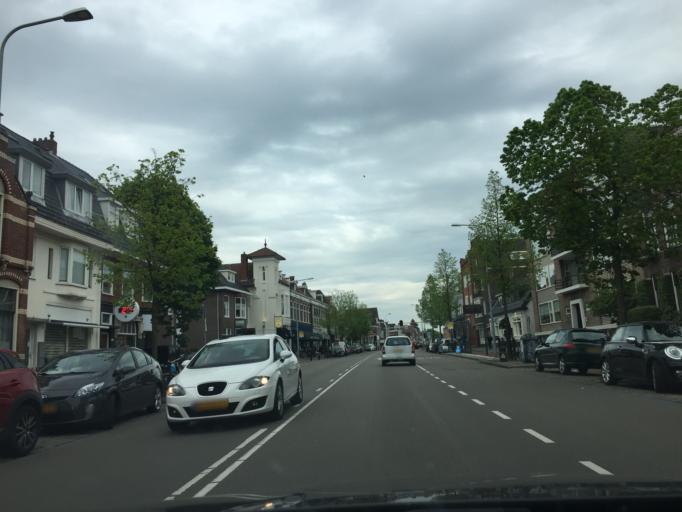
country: NL
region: Groningen
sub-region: Gemeente Groningen
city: Groningen
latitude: 53.2003
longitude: 6.5784
